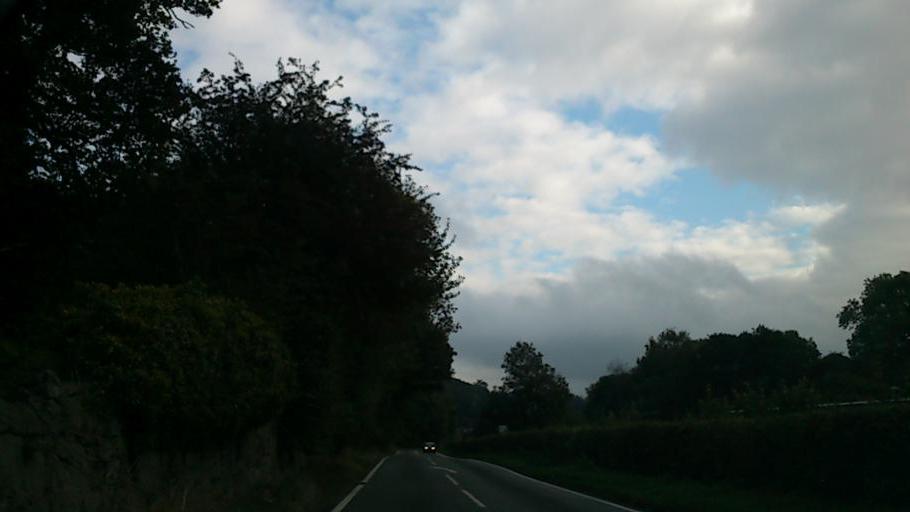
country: GB
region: Wales
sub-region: Sir Powys
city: Welshpool
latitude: 52.6587
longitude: -3.1620
